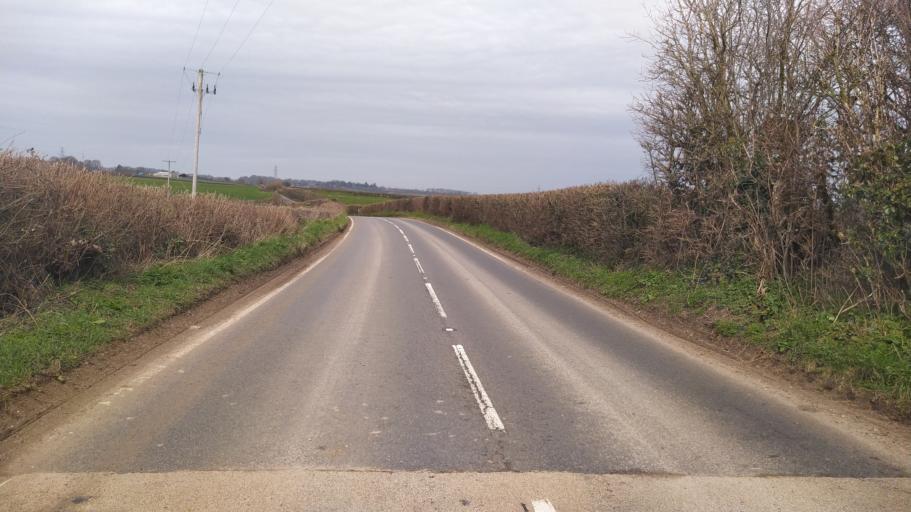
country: GB
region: England
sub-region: Somerset
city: Crewkerne
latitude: 50.8599
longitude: -2.7543
